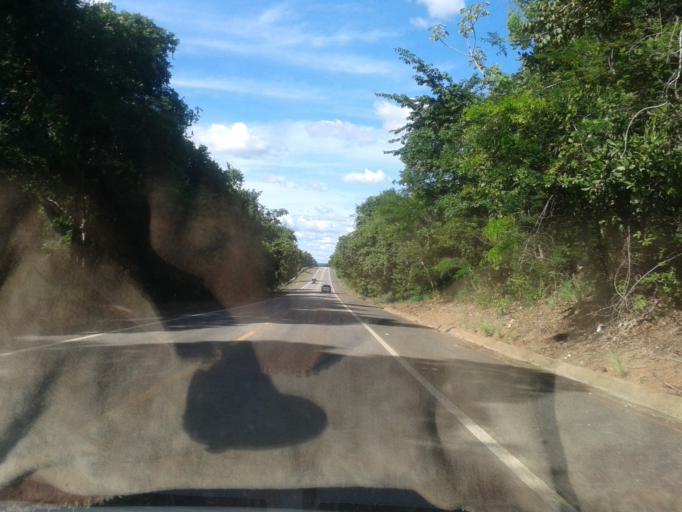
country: BR
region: Goias
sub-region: Mozarlandia
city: Mozarlandia
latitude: -15.0171
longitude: -50.5956
